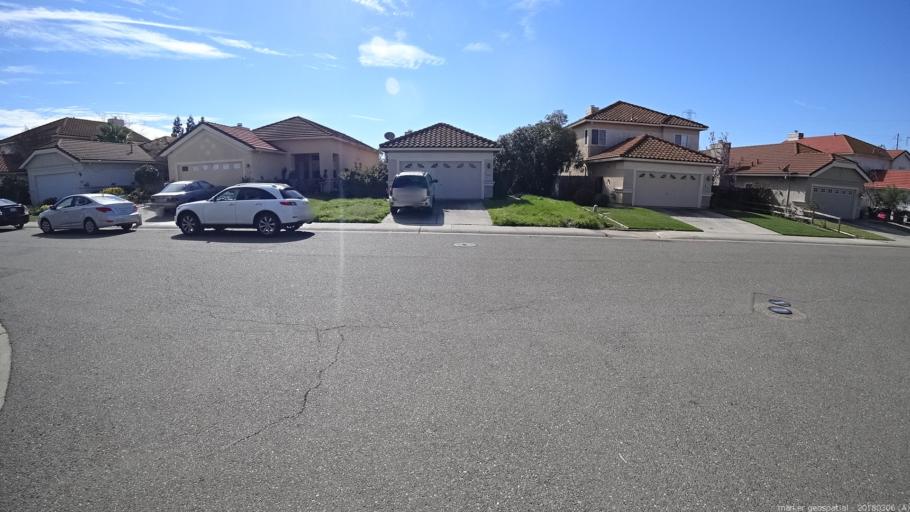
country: US
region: California
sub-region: Sacramento County
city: Vineyard
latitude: 38.4610
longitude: -121.3496
